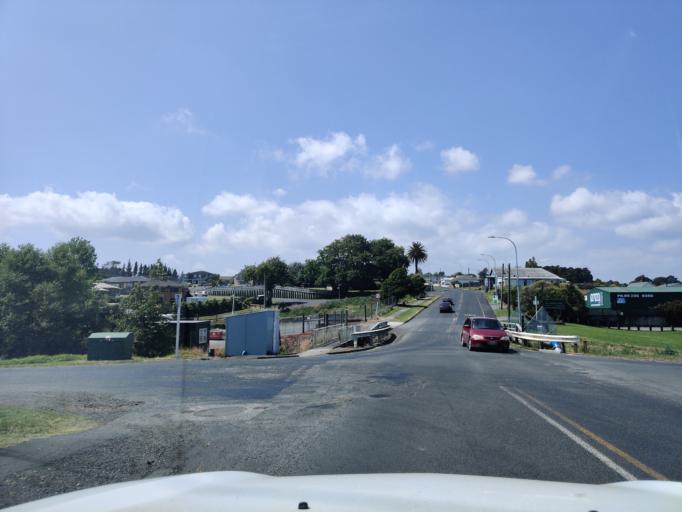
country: NZ
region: Auckland
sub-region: Auckland
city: Pukekohe East
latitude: -37.2565
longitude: 174.9475
